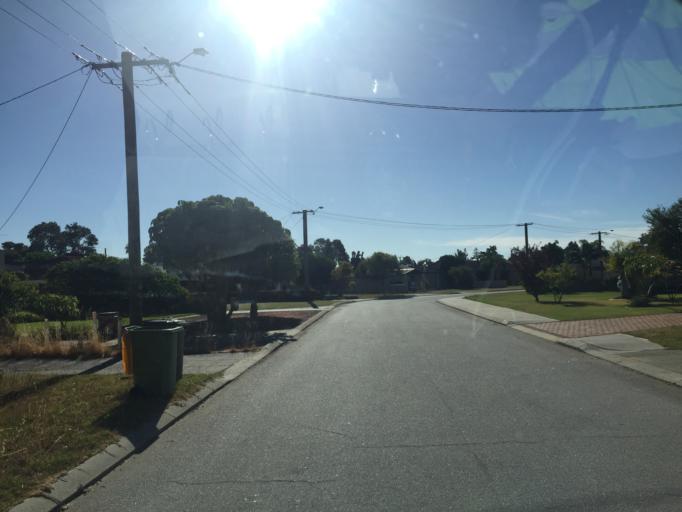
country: AU
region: Western Australia
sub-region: Canning
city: East Cannington
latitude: -32.0150
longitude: 115.9673
